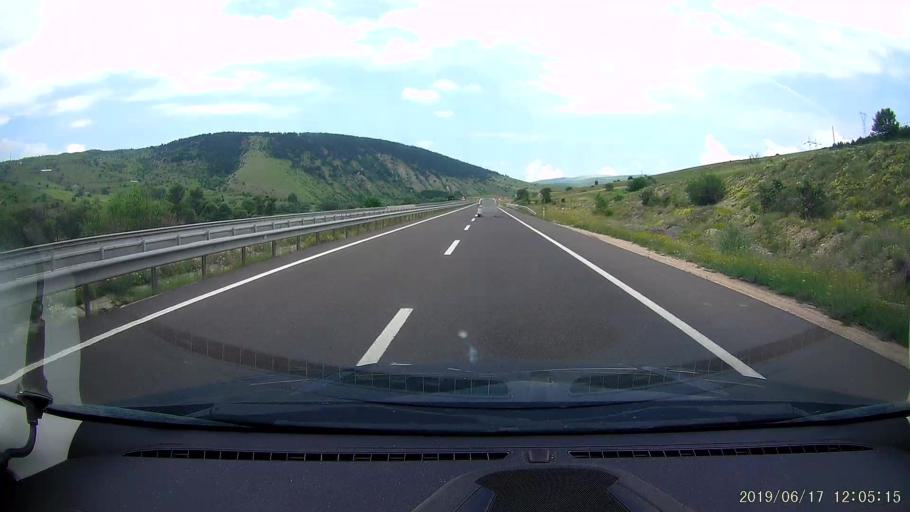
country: TR
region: Cankiri
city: Cerkes
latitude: 40.8297
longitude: 32.7821
